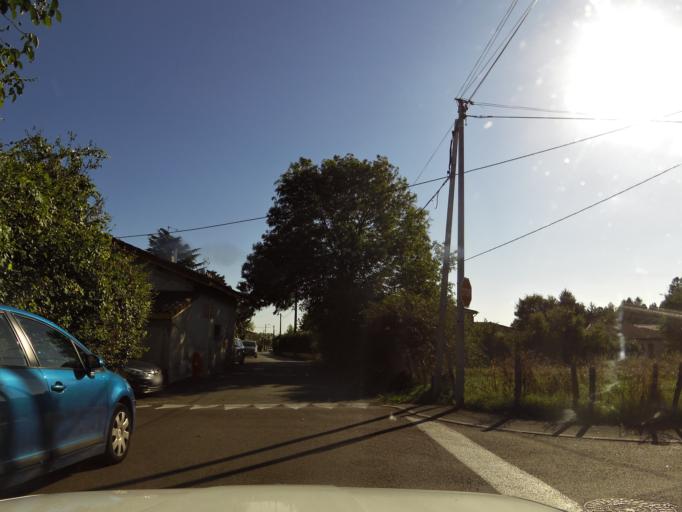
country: FR
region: Rhone-Alpes
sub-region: Departement de l'Ain
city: Meximieux
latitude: 45.9098
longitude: 5.2094
